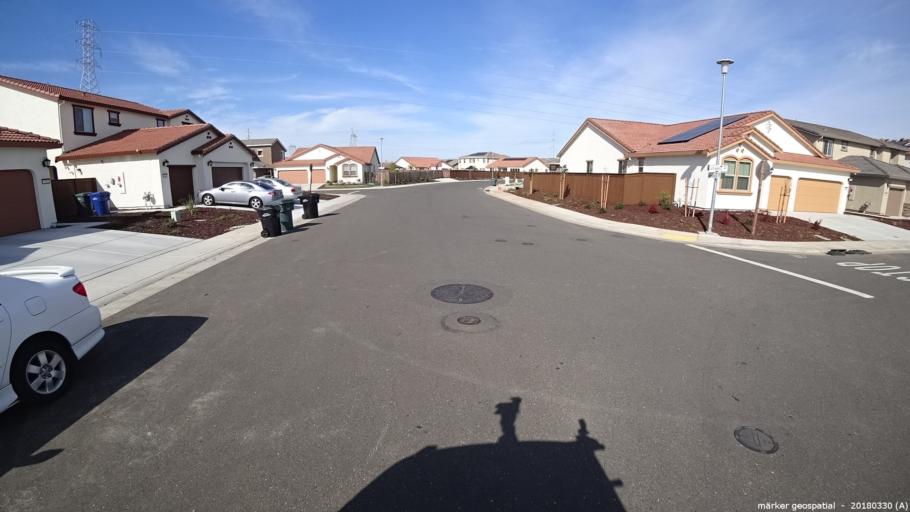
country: US
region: California
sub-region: Sacramento County
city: Vineyard
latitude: 38.4888
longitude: -121.3493
